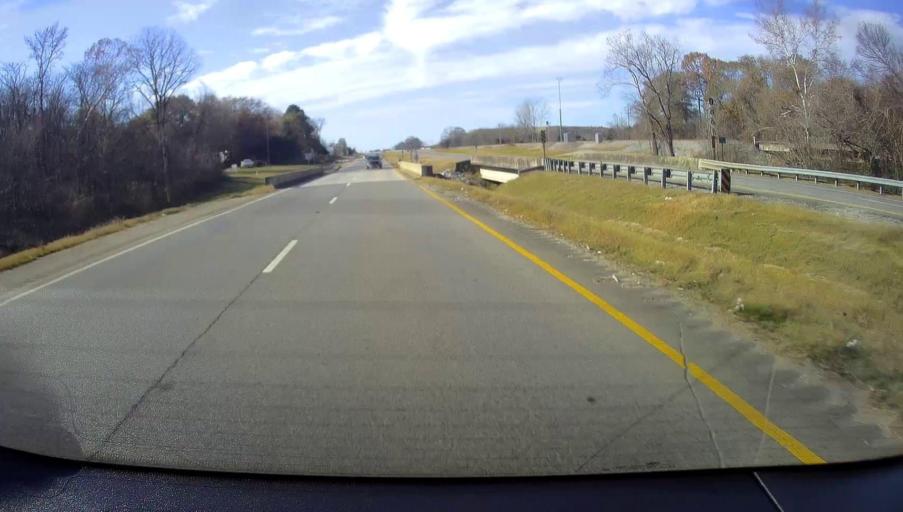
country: US
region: Alabama
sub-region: Colbert County
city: Tuscumbia
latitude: 34.7192
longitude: -87.7998
